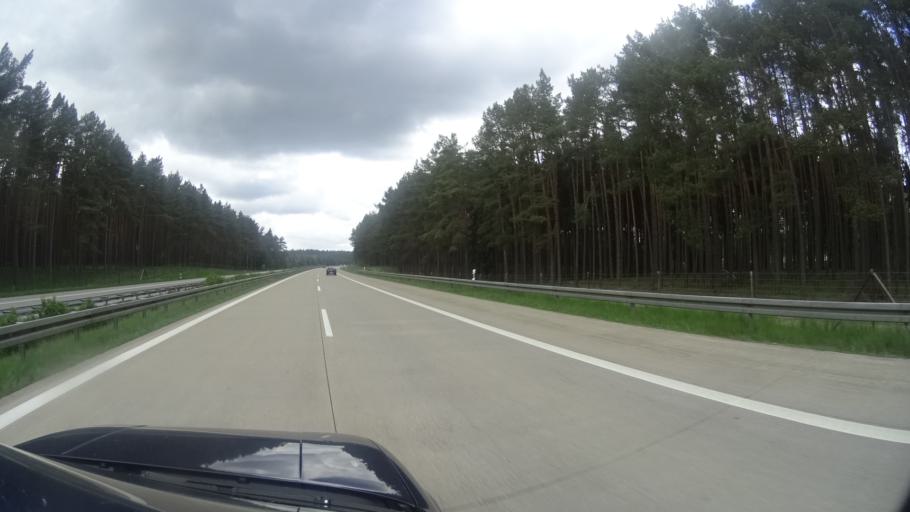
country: DE
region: Mecklenburg-Vorpommern
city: Plau am See
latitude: 53.5510
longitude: 12.3247
